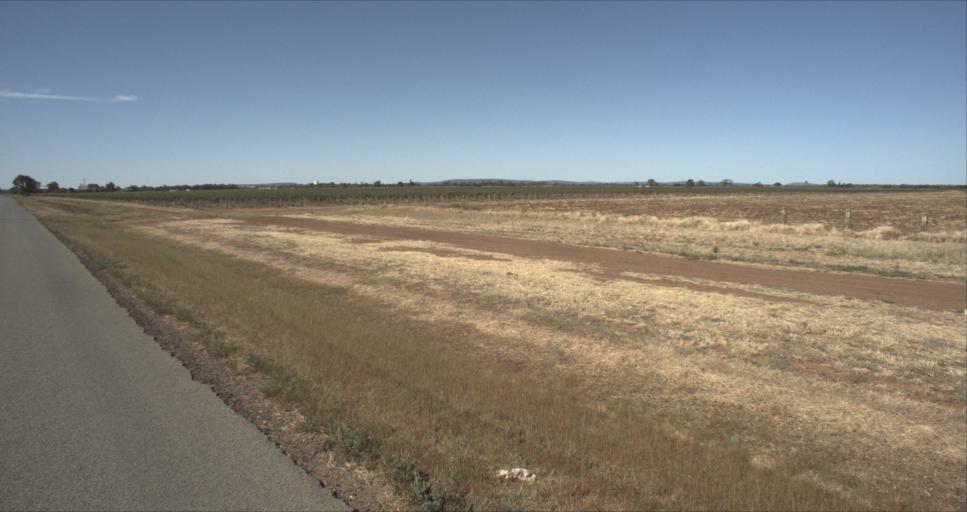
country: AU
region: New South Wales
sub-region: Leeton
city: Leeton
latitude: -34.5819
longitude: 146.3797
